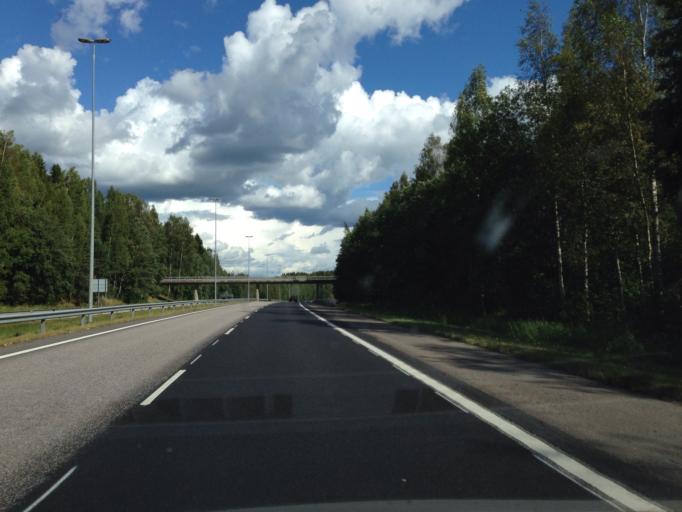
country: FI
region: Uusimaa
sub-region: Helsinki
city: Vihti
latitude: 60.2935
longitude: 24.3432
